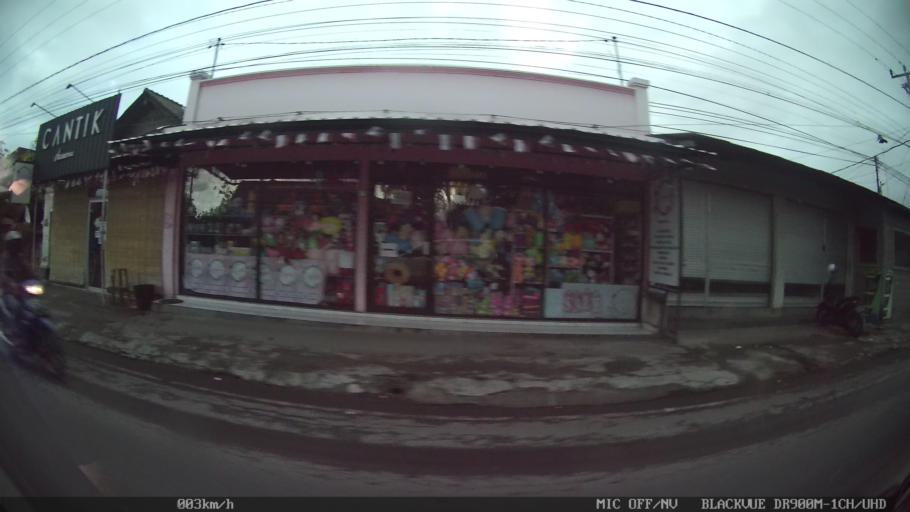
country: ID
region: Bali
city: Banjar Pasekan
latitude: -8.6109
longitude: 115.2836
